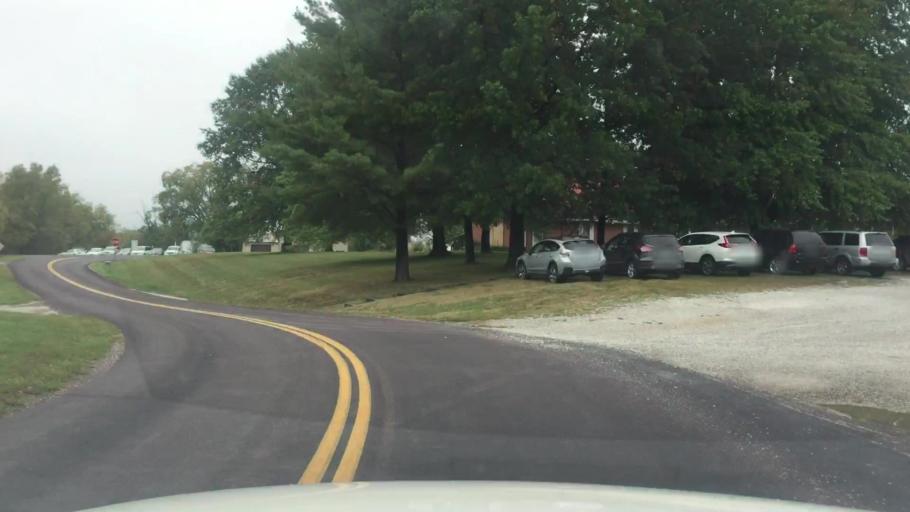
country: US
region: Missouri
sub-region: Boone County
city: Ashland
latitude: 38.8251
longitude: -92.3502
